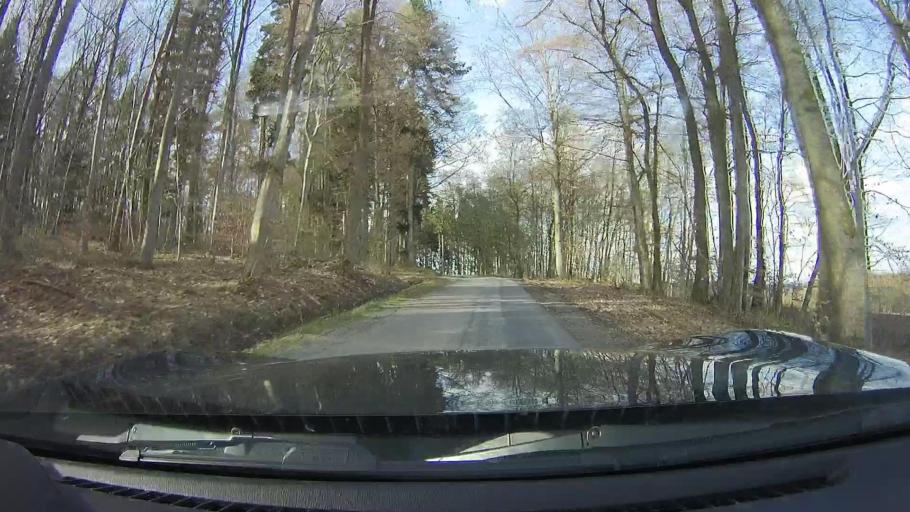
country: DE
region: Baden-Wuerttemberg
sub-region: Karlsruhe Region
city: Walldurn
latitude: 49.6033
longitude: 9.2825
